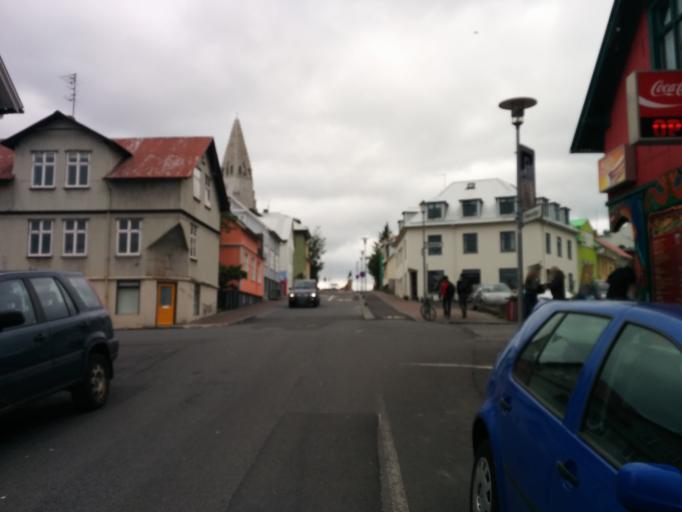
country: IS
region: Capital Region
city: Reykjavik
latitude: 64.1440
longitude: -21.9260
